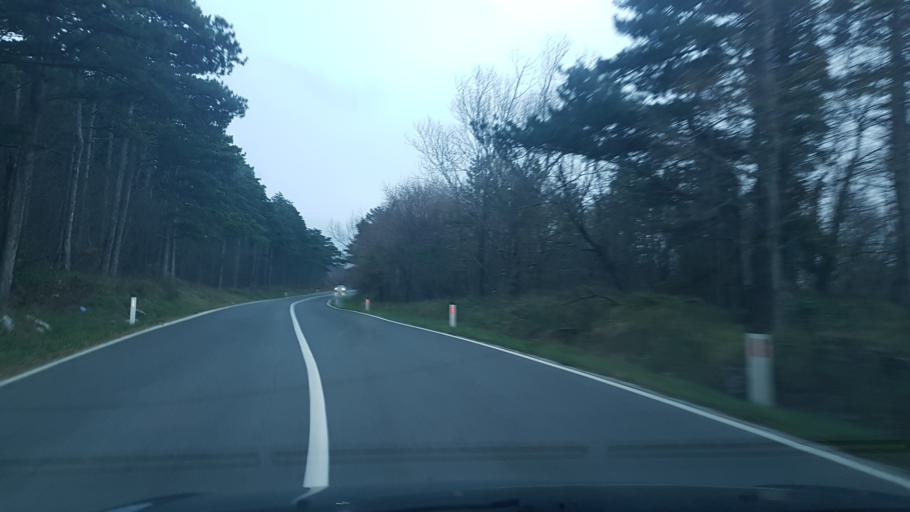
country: SI
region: Ajdovscina
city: Ajdovscina
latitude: 45.8854
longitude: 13.9253
